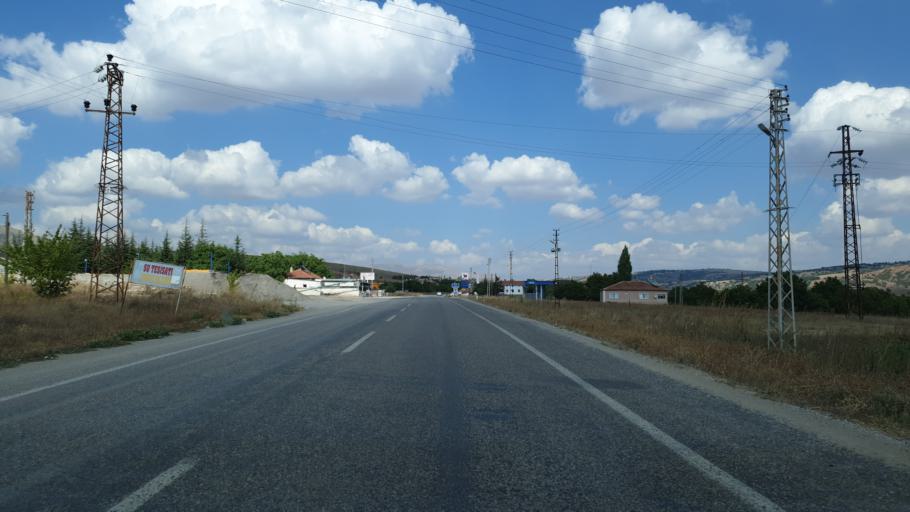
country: TR
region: Kayseri
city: Felahiye
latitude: 39.0991
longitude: 35.5847
